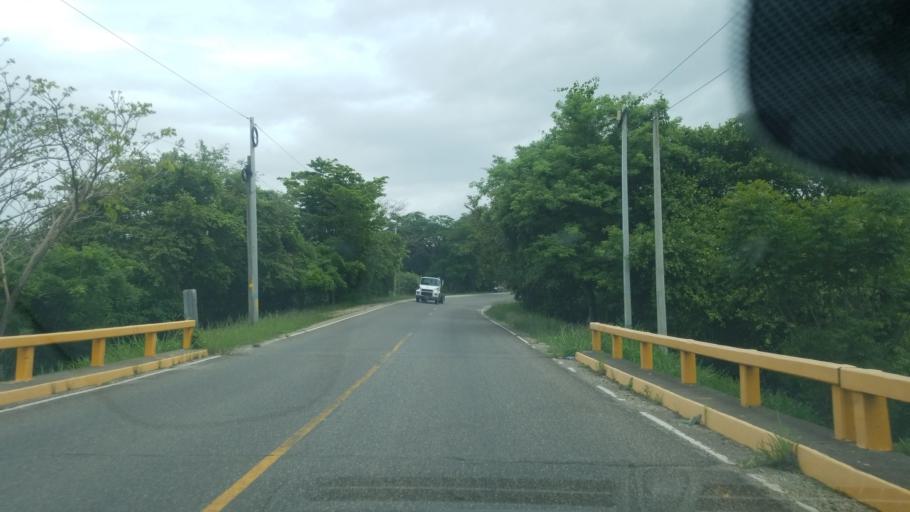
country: HN
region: Ocotepeque
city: Lucerna
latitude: 14.5214
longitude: -88.9491
